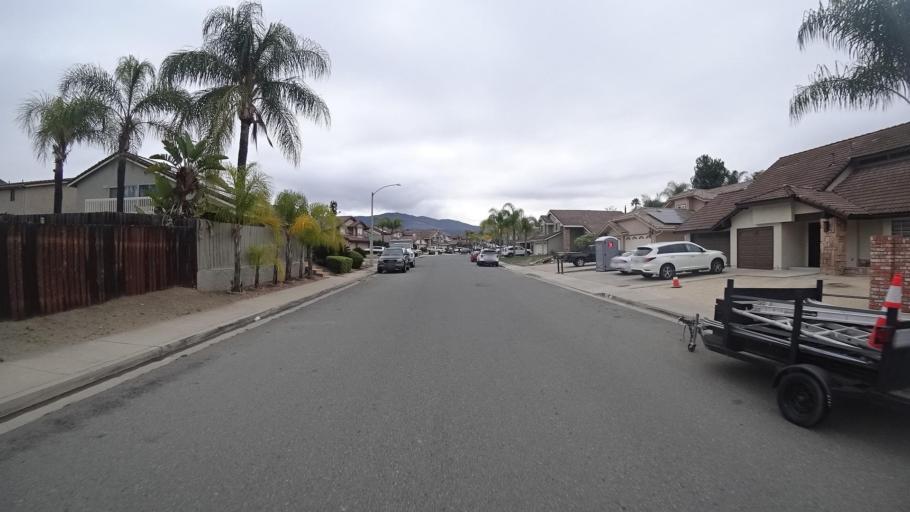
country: US
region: California
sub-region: San Diego County
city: Rancho San Diego
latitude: 32.7598
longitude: -116.9093
